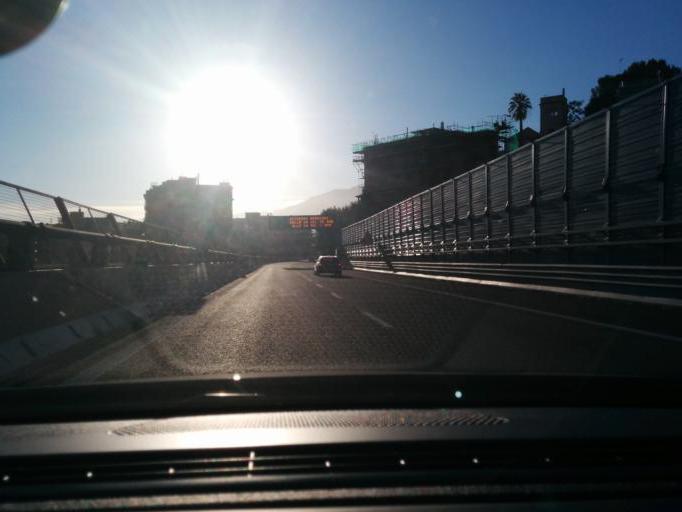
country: IT
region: Liguria
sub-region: Provincia di Genova
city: Mele
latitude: 44.4302
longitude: 8.7770
